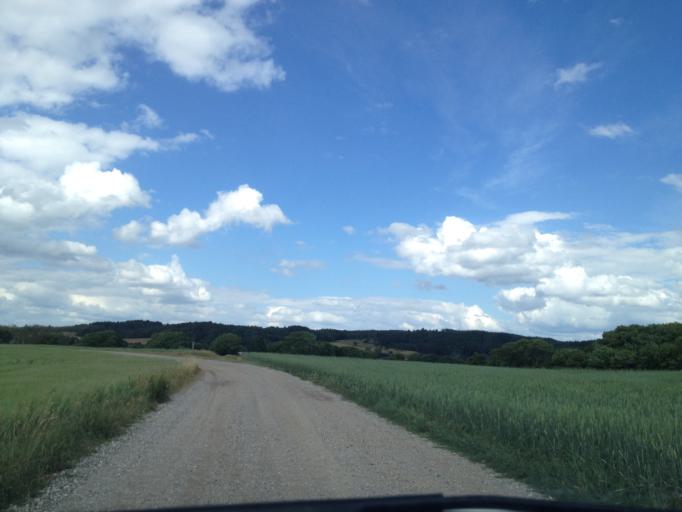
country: DK
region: Central Jutland
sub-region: Syddjurs Kommune
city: Ronde
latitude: 56.2017
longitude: 10.4839
